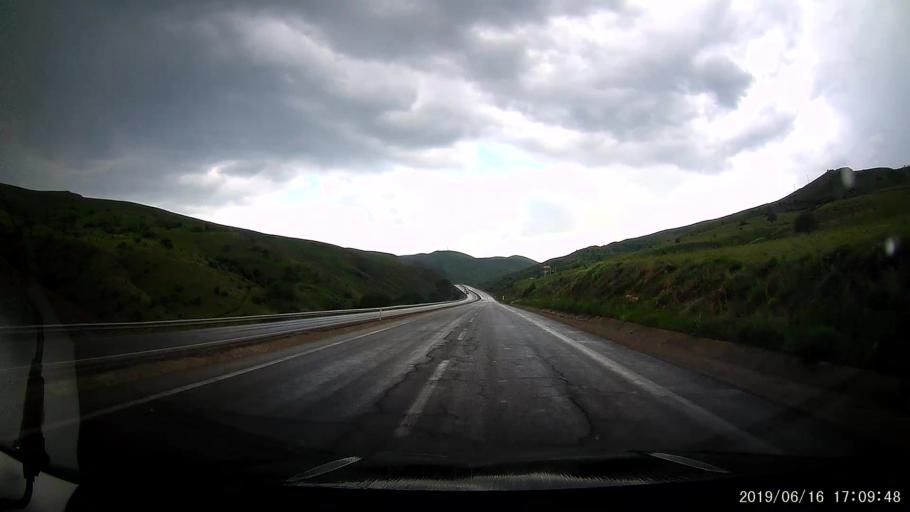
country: TR
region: Erzurum
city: Askale
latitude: 39.8891
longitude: 40.6478
